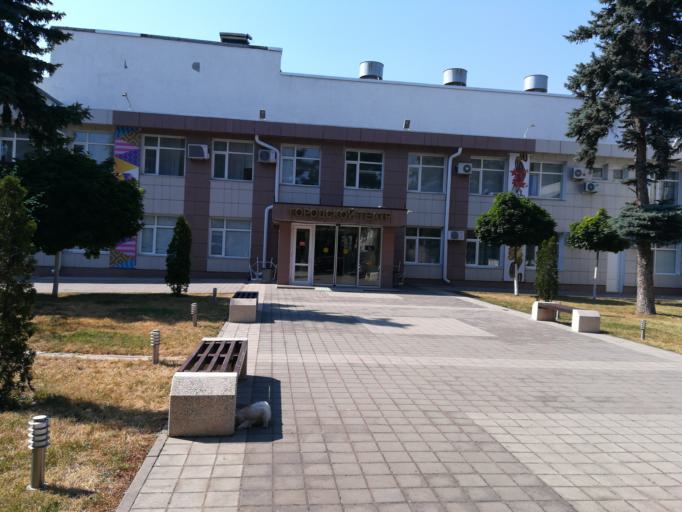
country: RU
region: Krasnodarskiy
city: Anapa
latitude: 44.8959
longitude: 37.3203
